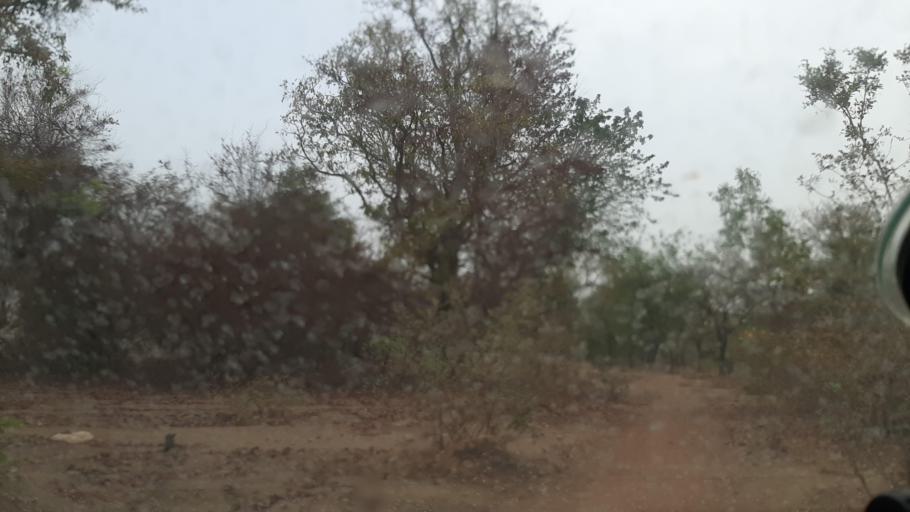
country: BF
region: Boucle du Mouhoun
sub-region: Province des Banwa
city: Salanso
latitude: 11.8512
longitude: -4.4267
